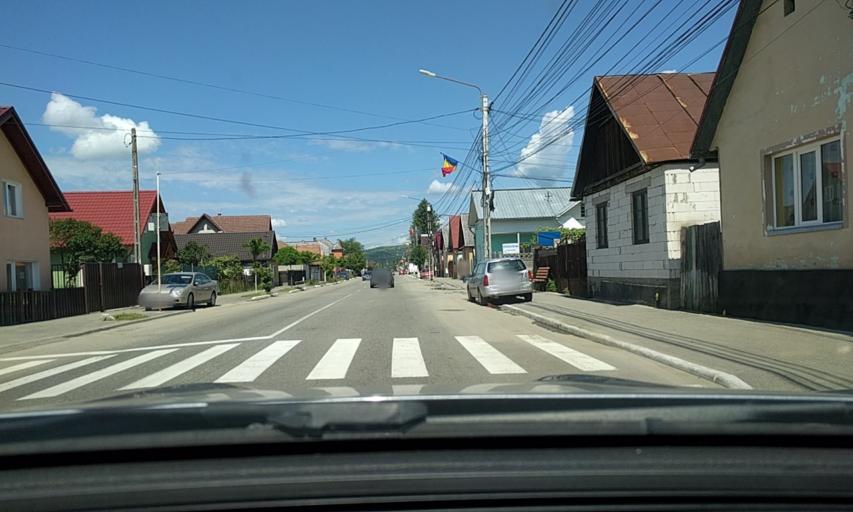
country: RO
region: Bistrita-Nasaud
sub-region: Oras Nasaud
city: Nasaud
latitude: 47.2909
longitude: 24.3898
